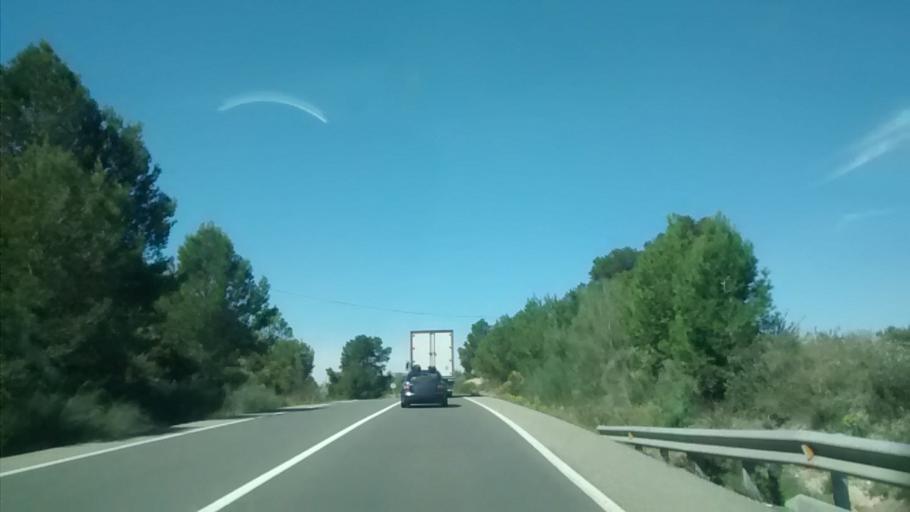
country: ES
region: Catalonia
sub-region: Provincia de Tarragona
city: Ginestar
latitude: 41.0476
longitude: 0.6537
